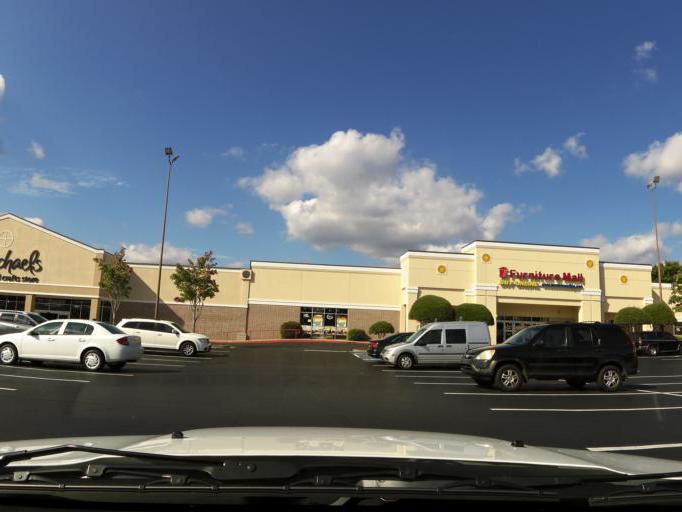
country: US
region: Georgia
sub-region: Cobb County
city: Kennesaw
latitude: 34.0113
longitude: -84.5714
